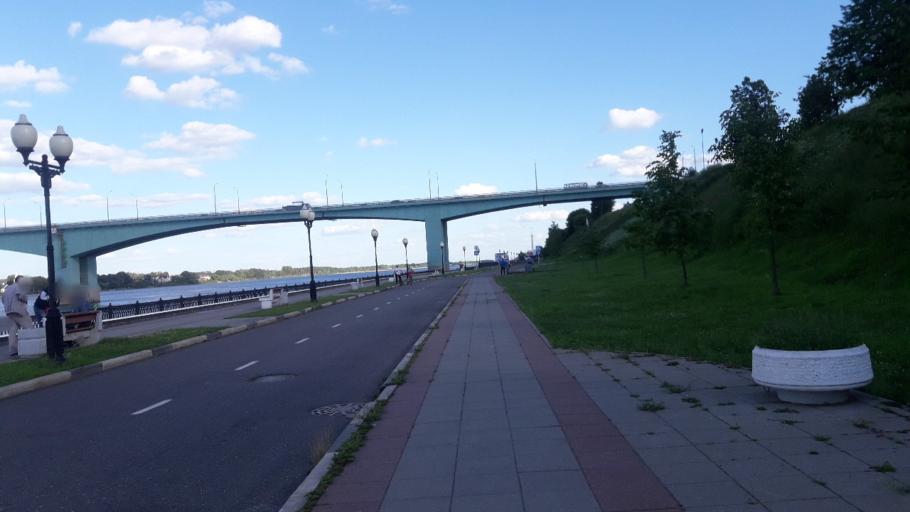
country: RU
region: Jaroslavl
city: Yaroslavl
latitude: 57.6415
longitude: 39.8869
